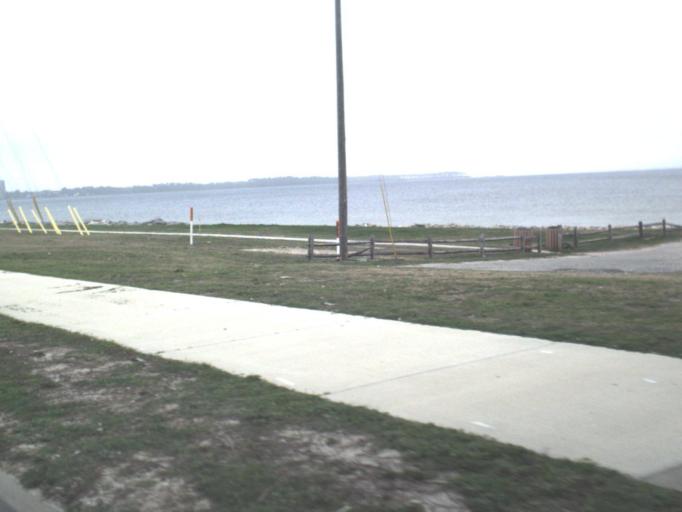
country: US
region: Florida
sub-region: Bay County
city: Upper Grand Lagoon
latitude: 30.1865
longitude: -85.7334
